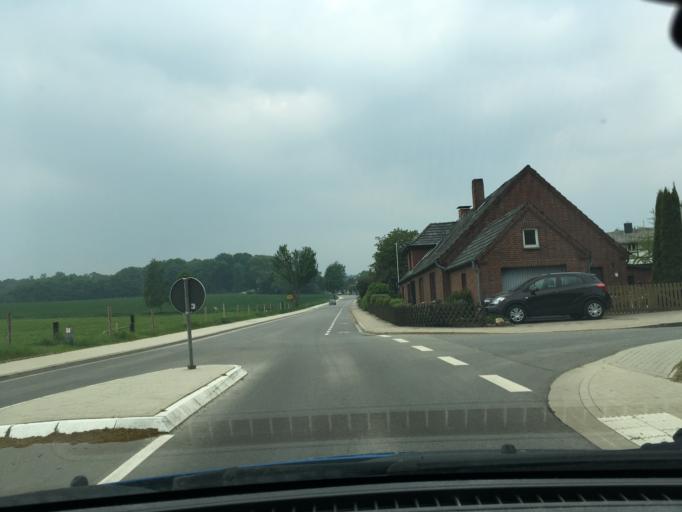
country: DE
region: Lower Saxony
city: Seevetal
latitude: 53.4066
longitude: 9.8957
